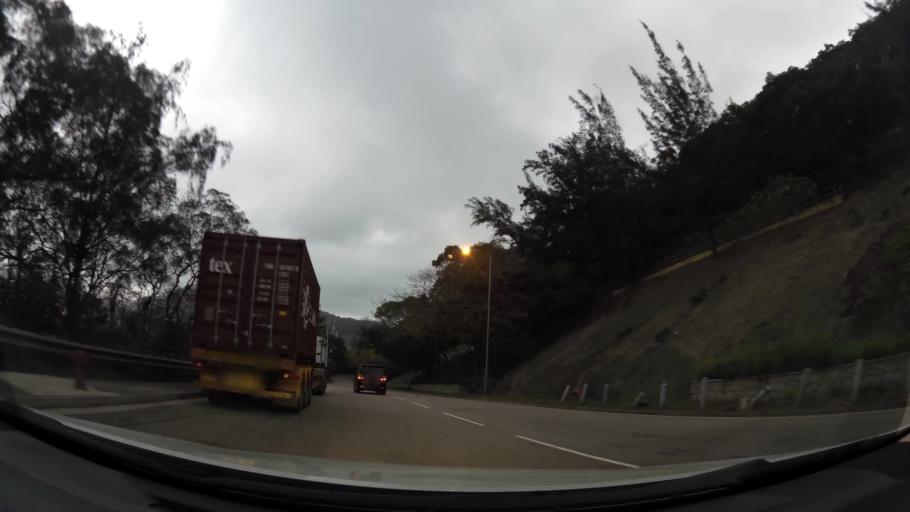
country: HK
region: Tsuen Wan
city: Tsuen Wan
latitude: 22.3338
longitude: 114.0917
